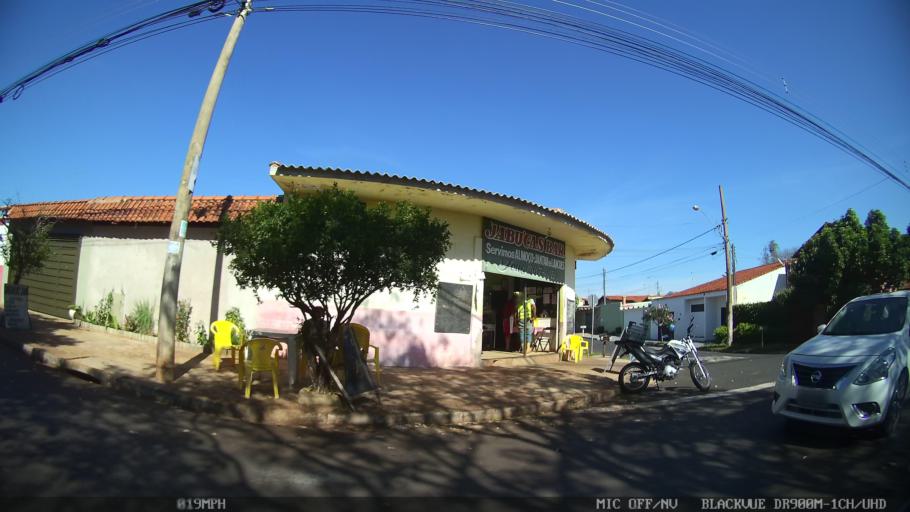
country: BR
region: Sao Paulo
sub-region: Ribeirao Preto
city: Ribeirao Preto
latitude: -21.2238
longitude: -47.7656
